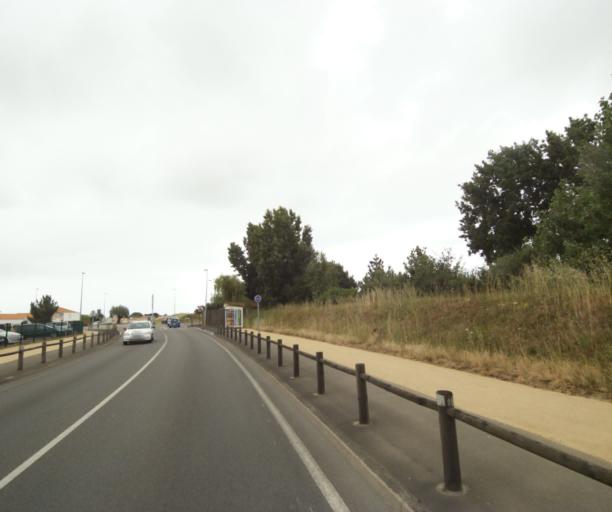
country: FR
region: Pays de la Loire
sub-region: Departement de la Vendee
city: Chateau-d'Olonne
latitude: 46.5027
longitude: -1.7593
